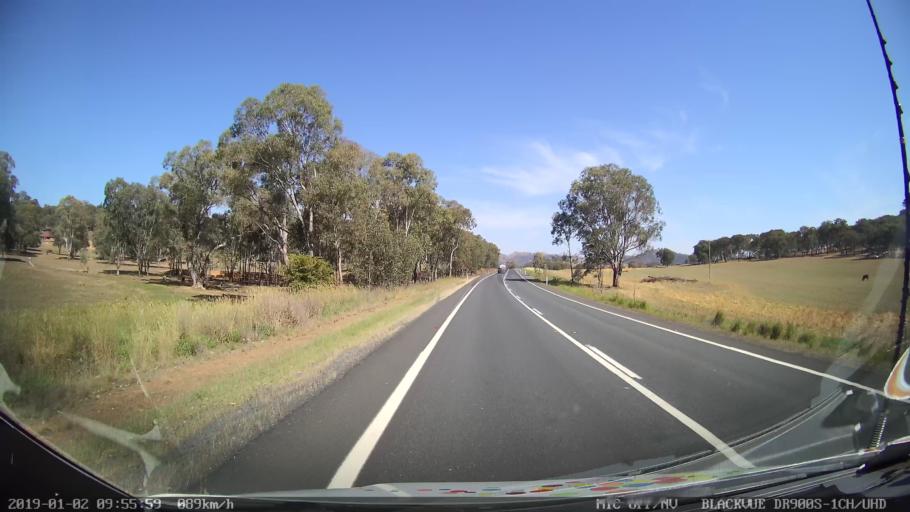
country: AU
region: New South Wales
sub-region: Tumut Shire
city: Tumut
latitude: -35.2193
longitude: 148.1814
